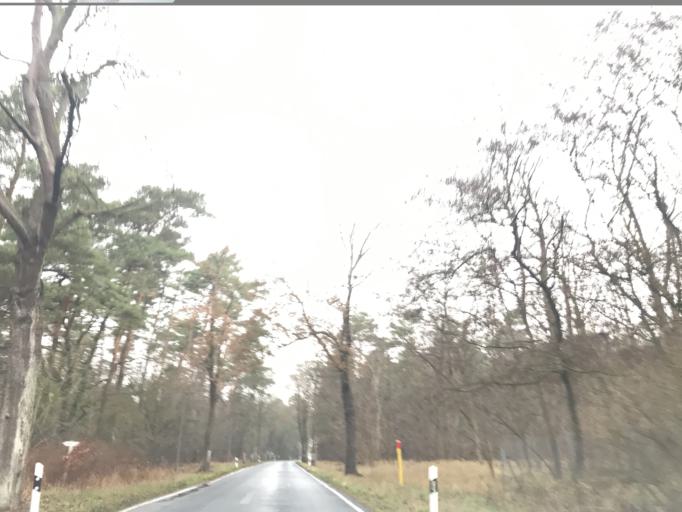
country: DE
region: Brandenburg
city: Brieselang
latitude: 52.6625
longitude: 12.9813
